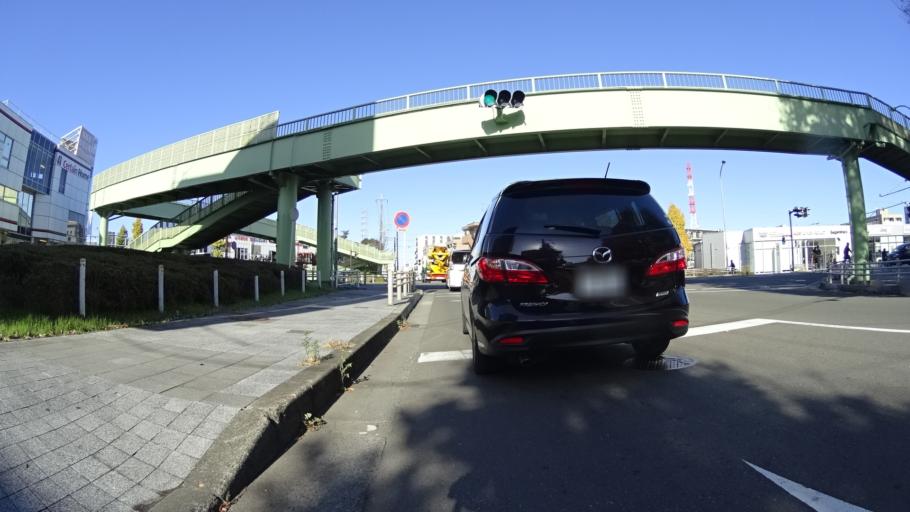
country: JP
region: Tokyo
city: Hachioji
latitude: 35.5788
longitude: 139.3612
